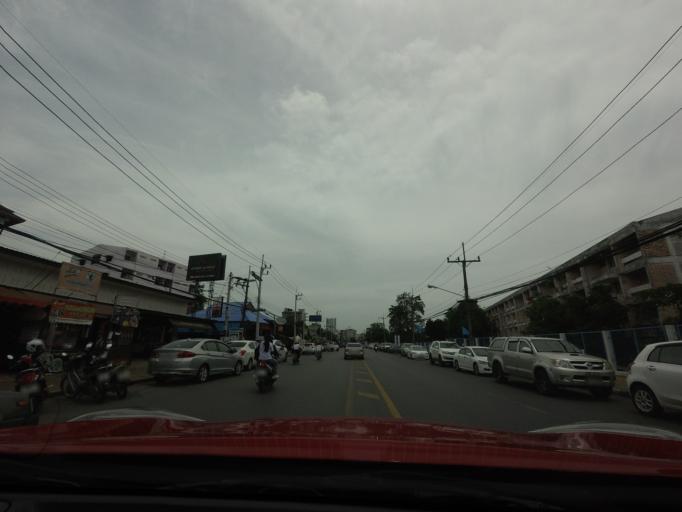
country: TH
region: Songkhla
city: Hat Yai
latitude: 7.0018
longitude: 100.4941
